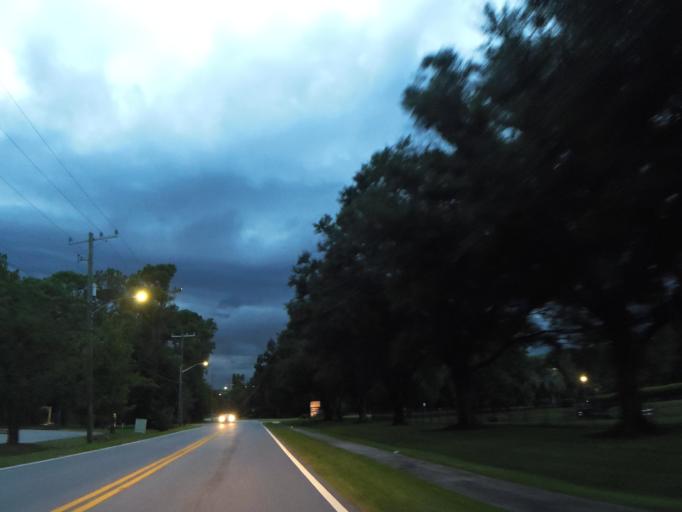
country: US
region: Florida
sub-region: Duval County
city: Jacksonville
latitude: 30.2709
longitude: -81.6166
